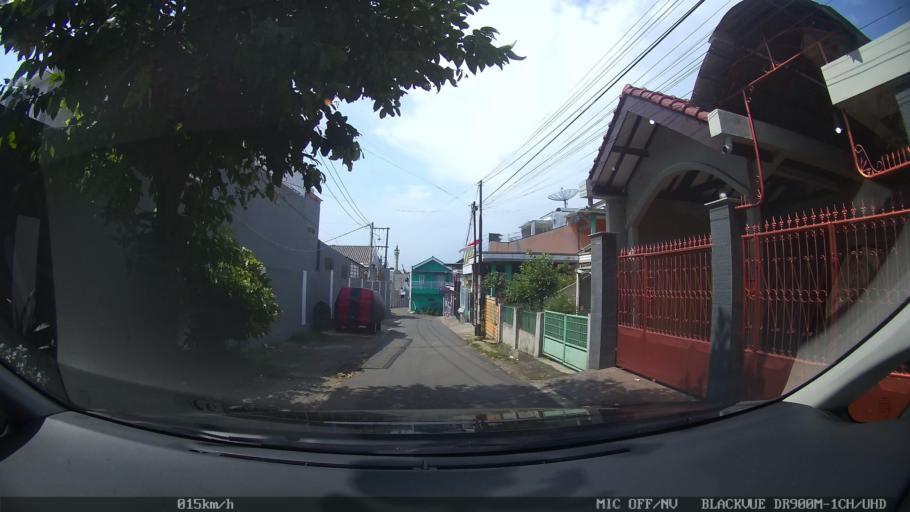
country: ID
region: Lampung
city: Kedaton
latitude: -5.3947
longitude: 105.2441
